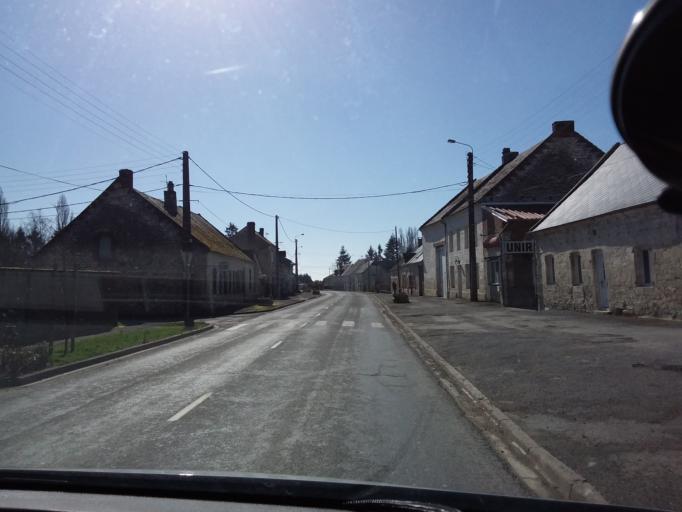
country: FR
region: Picardie
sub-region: Departement de l'Aisne
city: Montcornet
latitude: 49.6262
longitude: 4.0227
